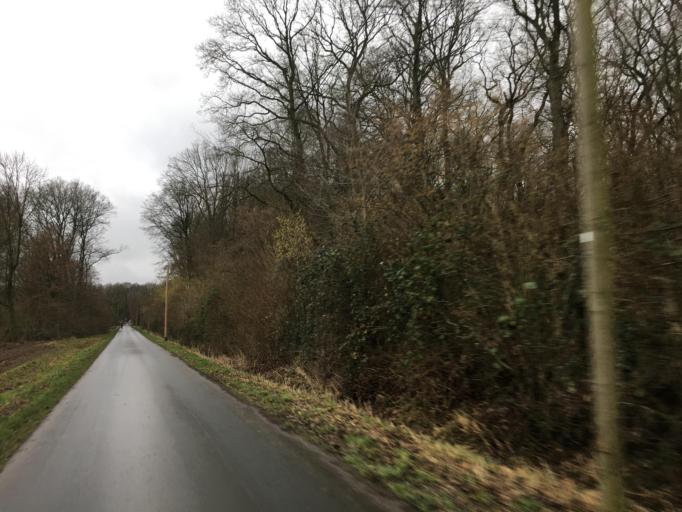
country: DE
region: North Rhine-Westphalia
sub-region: Regierungsbezirk Munster
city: Muenster
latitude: 51.9286
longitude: 7.5484
